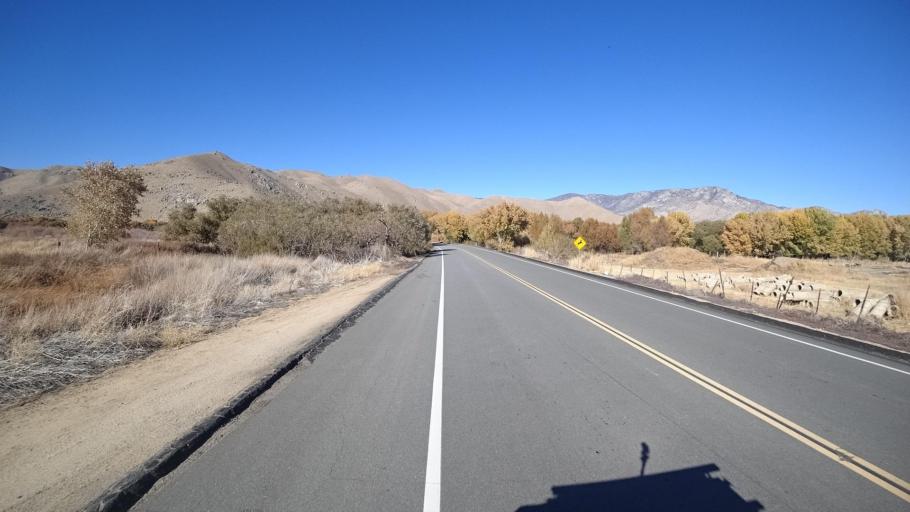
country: US
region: California
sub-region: Kern County
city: Weldon
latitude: 35.6672
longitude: -118.3227
